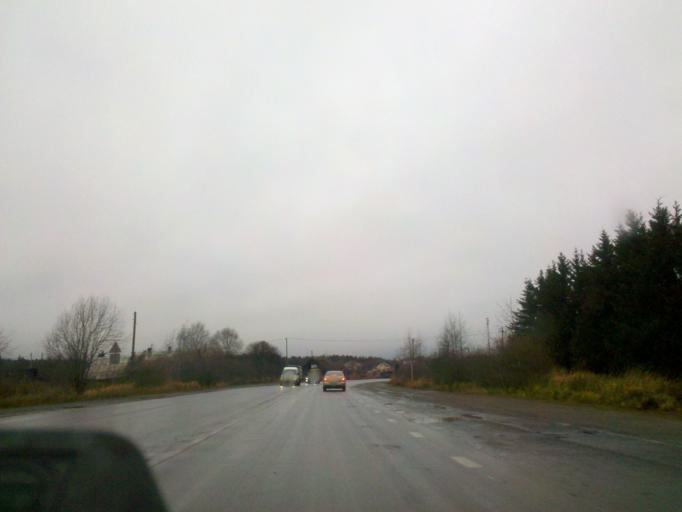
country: RU
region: Republic of Karelia
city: Shuya
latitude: 61.8615
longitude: 34.1614
